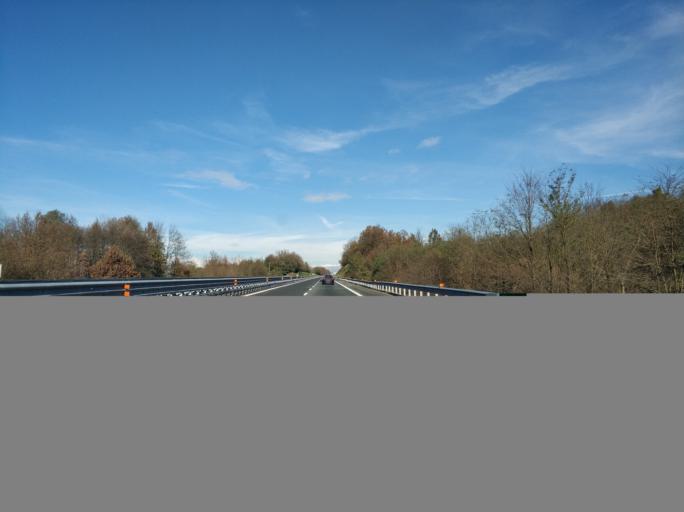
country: IT
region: Piedmont
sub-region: Provincia di Torino
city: San Giusto Canavese
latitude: 45.2983
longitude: 7.8165
